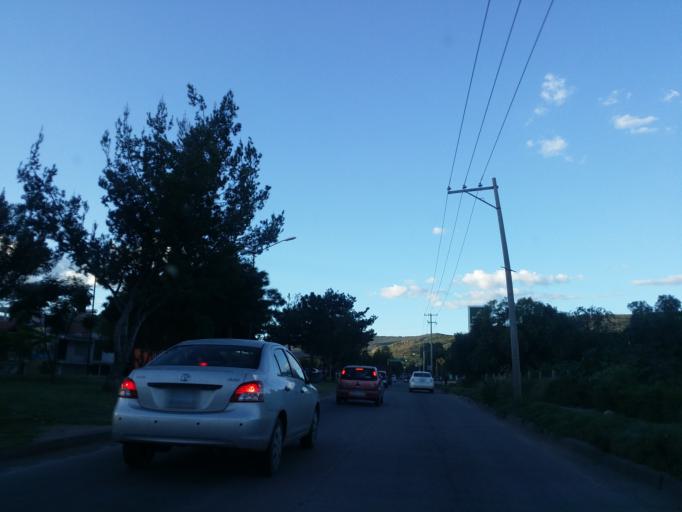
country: MX
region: Guanajuato
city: Leon
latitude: 21.1803
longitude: -101.6640
